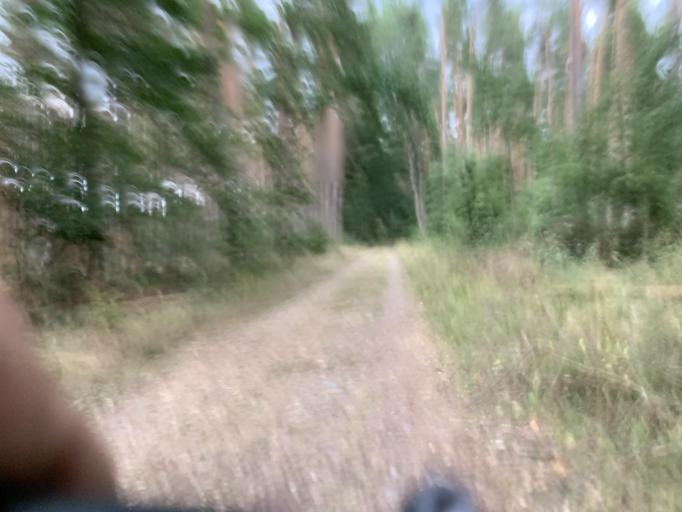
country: DE
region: Lower Saxony
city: Reinstorf
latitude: 53.2202
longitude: 10.6147
